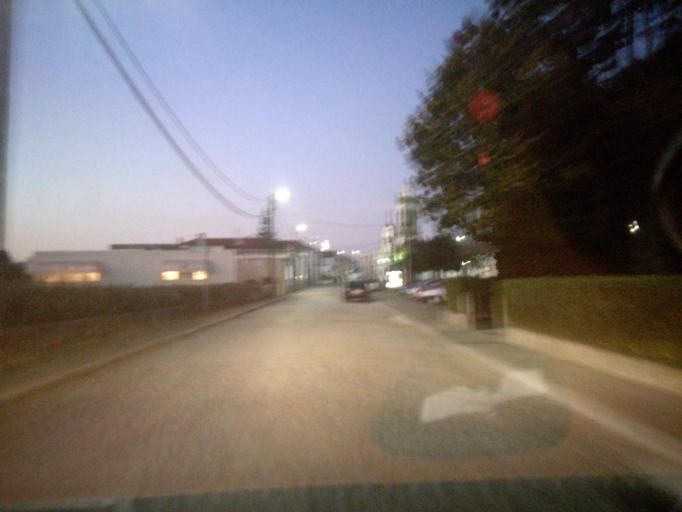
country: PT
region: Porto
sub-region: Maia
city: Nogueira
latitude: 41.2382
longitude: -8.5872
